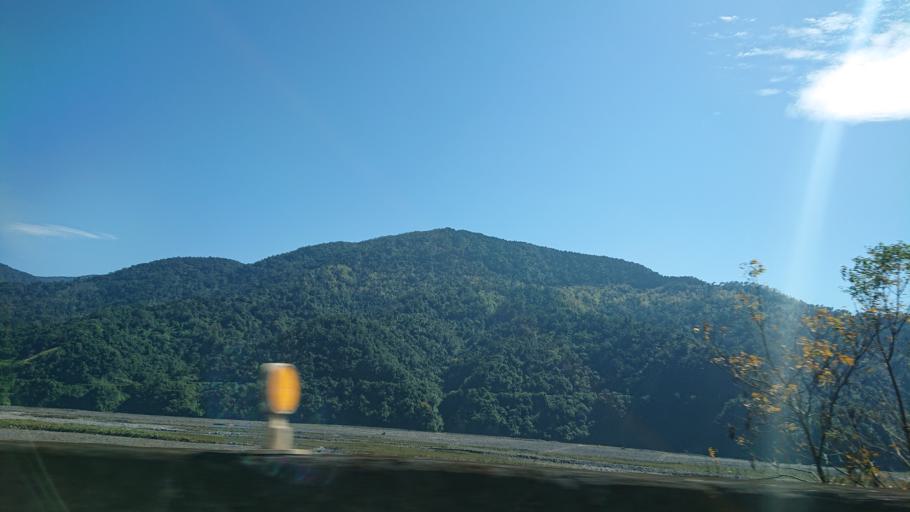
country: TW
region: Taiwan
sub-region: Yilan
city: Yilan
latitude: 24.5872
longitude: 121.5029
